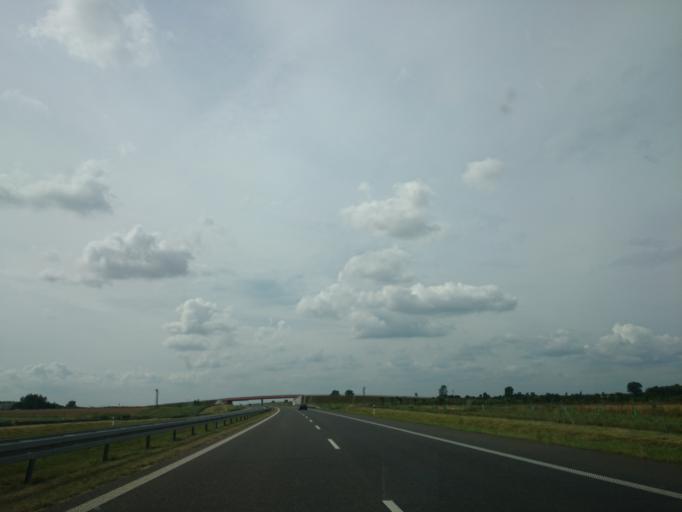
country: PL
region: West Pomeranian Voivodeship
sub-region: Powiat pyrzycki
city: Kozielice
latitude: 53.0967
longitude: 14.8147
